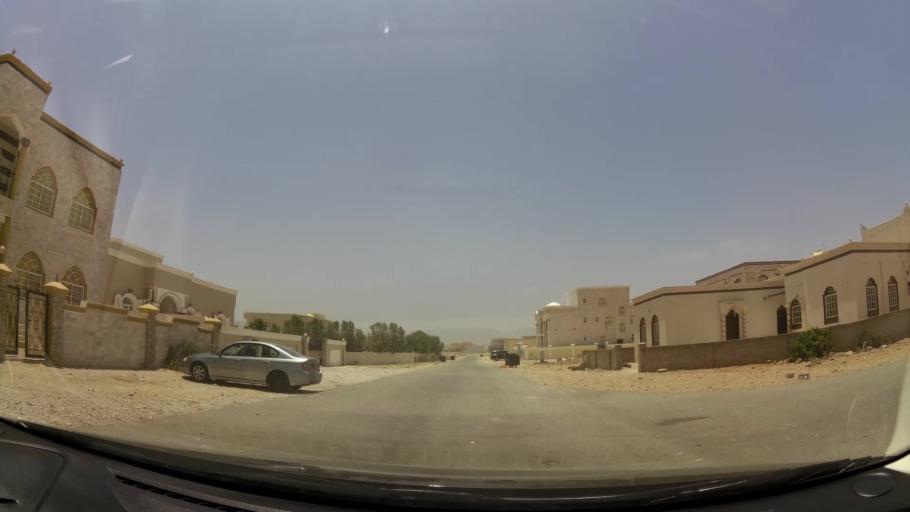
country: OM
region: Zufar
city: Salalah
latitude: 17.0927
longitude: 54.1667
